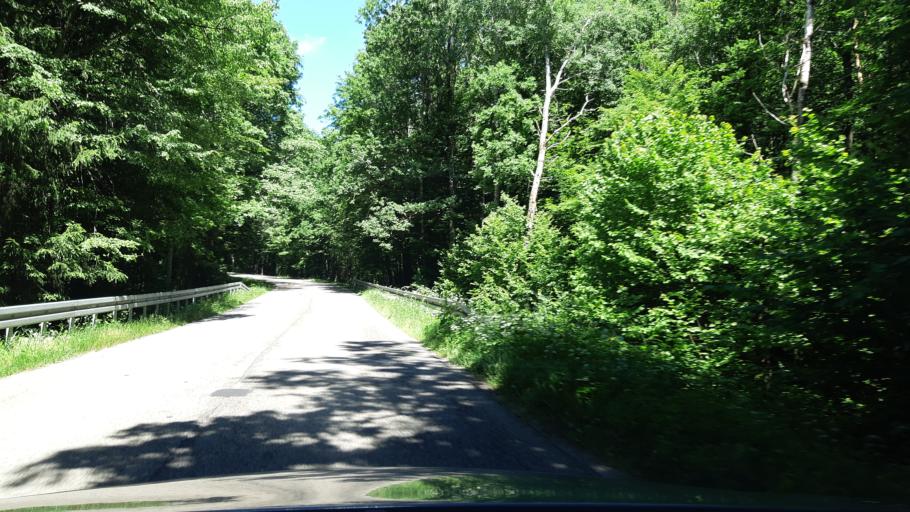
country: PL
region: Warmian-Masurian Voivodeship
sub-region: Powiat mragowski
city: Mikolajki
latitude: 53.7455
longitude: 21.5054
